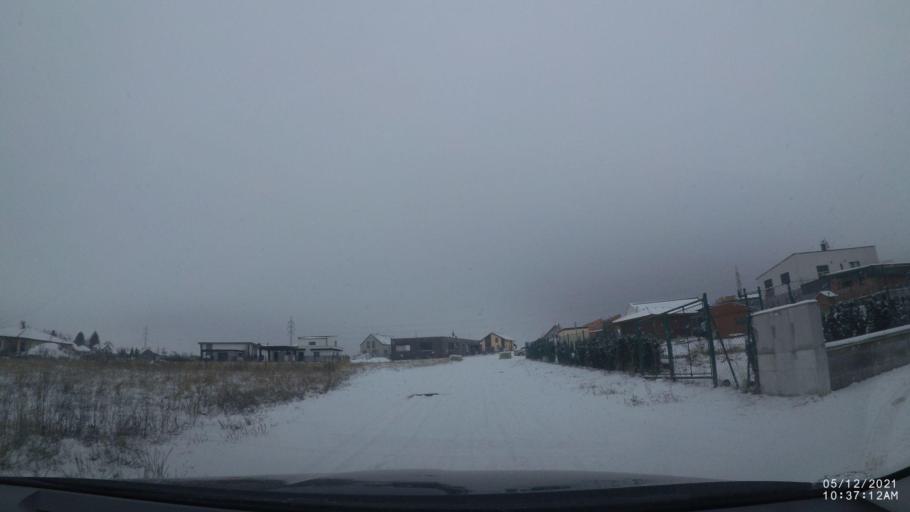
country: CZ
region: Kralovehradecky
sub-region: Okres Rychnov nad Kneznou
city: Rychnov nad Kneznou
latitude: 50.1654
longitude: 16.2903
